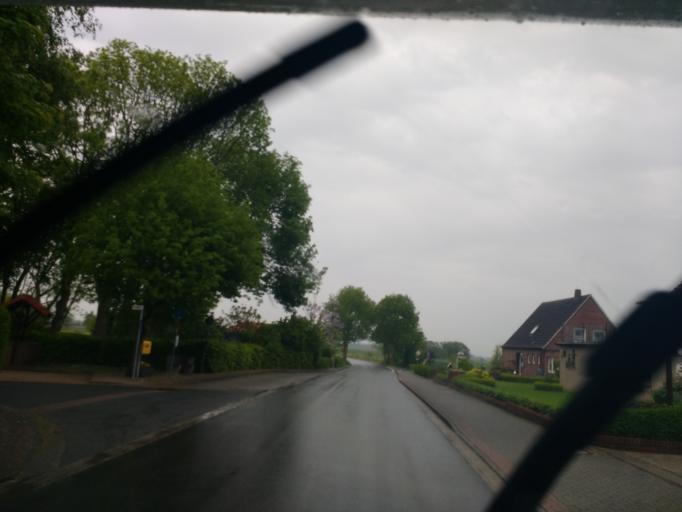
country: DE
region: Lower Saxony
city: Wangerooge
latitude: 53.6870
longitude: 7.8978
